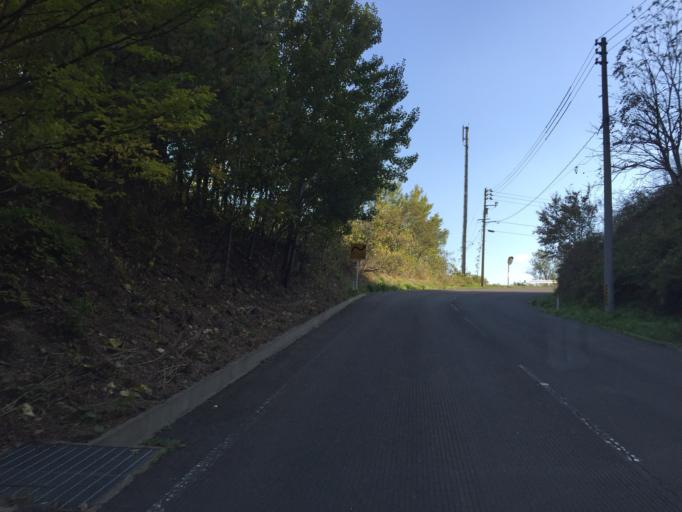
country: JP
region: Fukushima
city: Fukushima-shi
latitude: 37.8279
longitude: 140.3907
